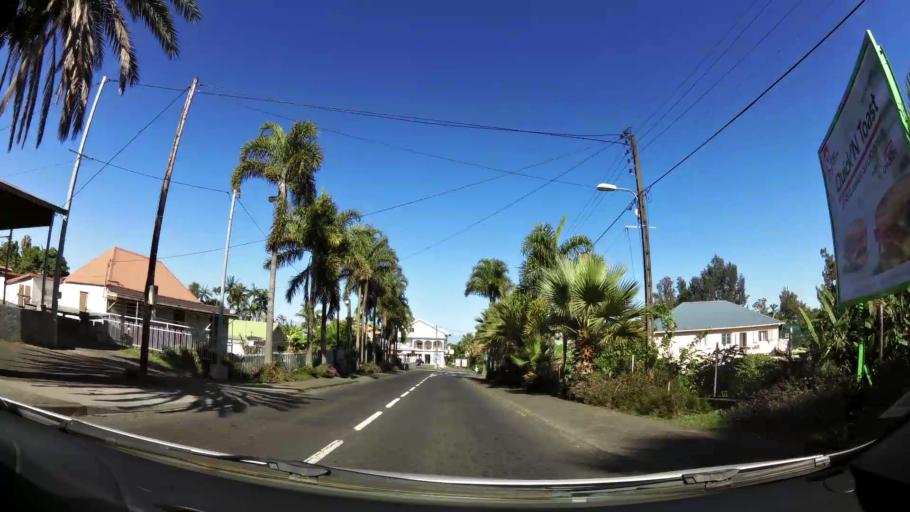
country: RE
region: Reunion
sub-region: Reunion
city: Le Tampon
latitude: -21.2669
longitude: 55.5246
